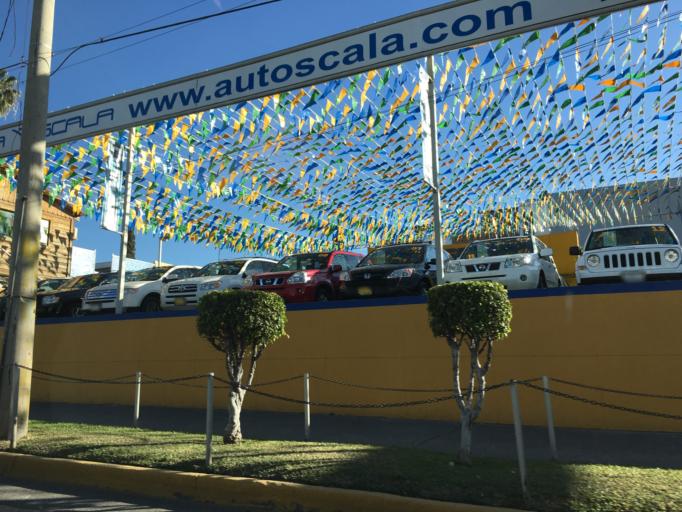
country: MX
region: Jalisco
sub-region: Zapopan
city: Zapopan
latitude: 20.7069
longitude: -103.3544
